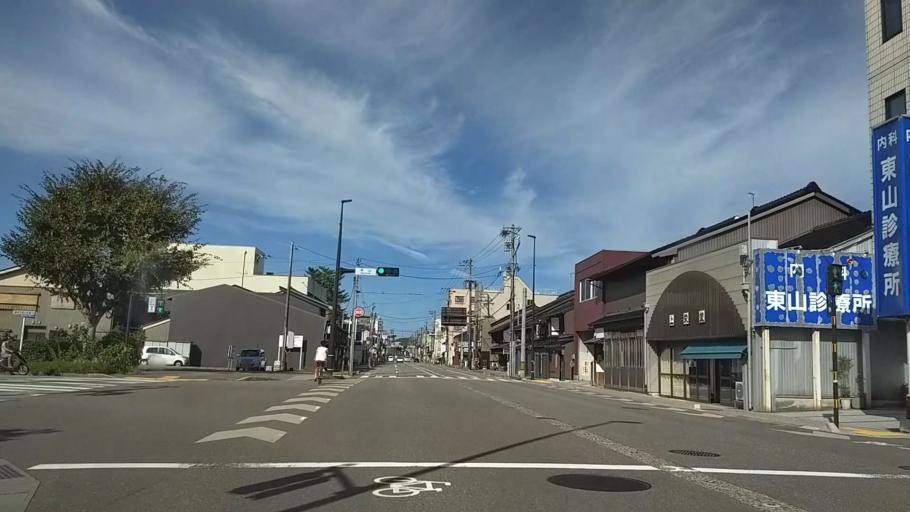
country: JP
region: Ishikawa
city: Kanazawa-shi
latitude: 36.5742
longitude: 136.6660
